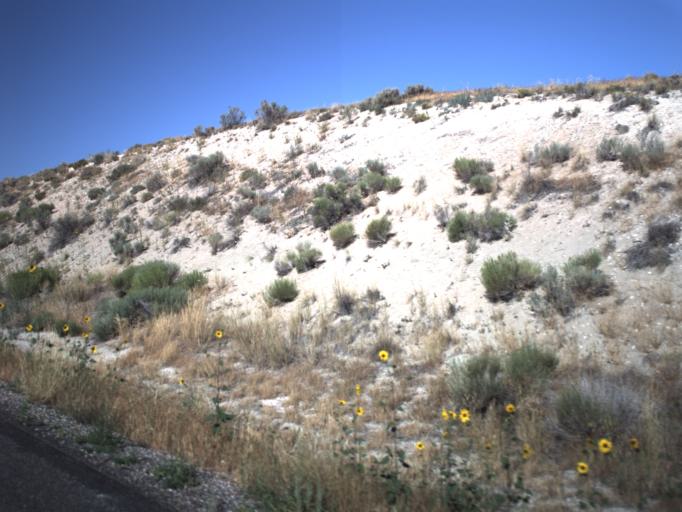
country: US
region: Utah
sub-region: Juab County
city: Mona
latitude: 39.7072
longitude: -112.2098
